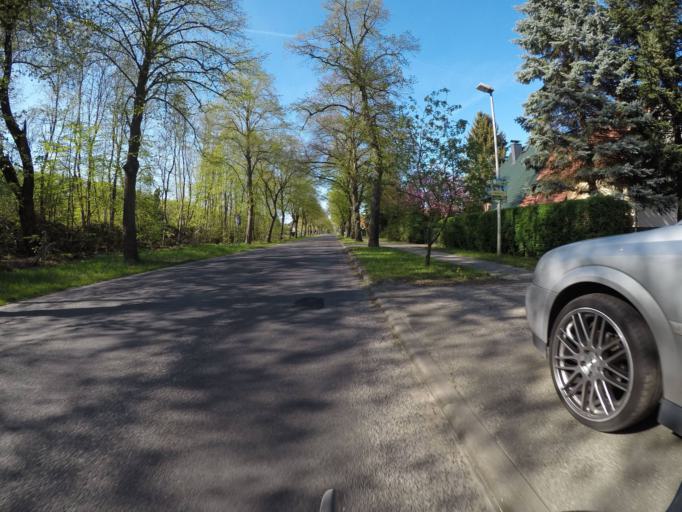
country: DE
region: Brandenburg
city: Rehfelde
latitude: 52.4723
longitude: 13.8550
